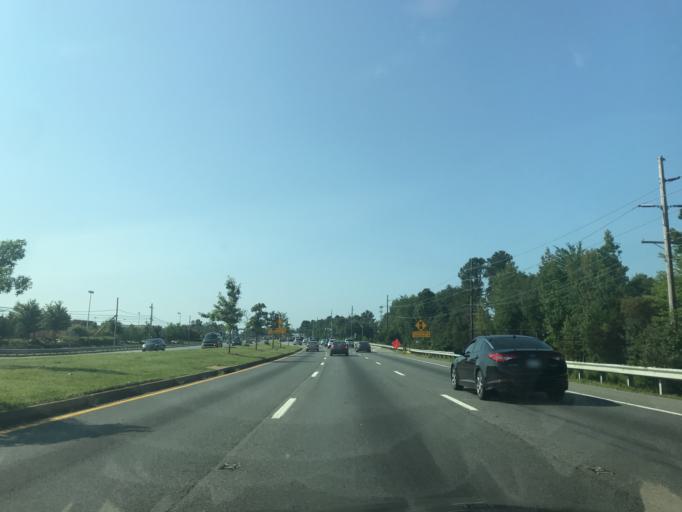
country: US
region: Maryland
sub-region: Prince George's County
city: Brandywine
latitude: 38.6775
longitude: -76.8756
